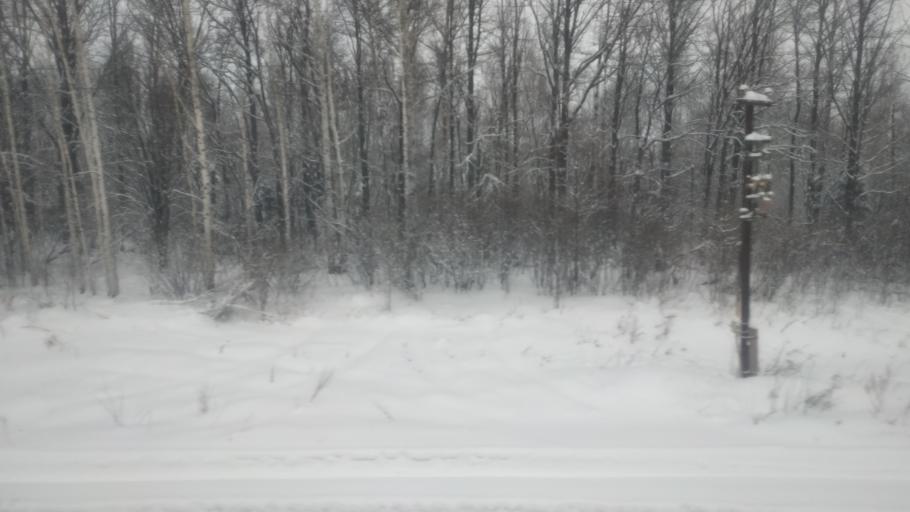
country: RU
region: Udmurtiya
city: Kiyasovo
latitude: 56.5028
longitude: 53.3605
